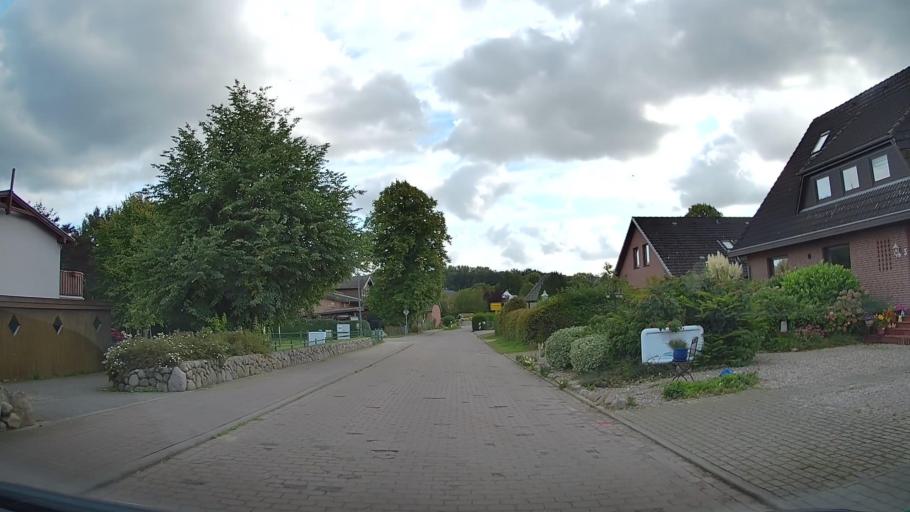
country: DE
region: Schleswig-Holstein
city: Steinberg
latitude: 54.7781
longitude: 9.7997
